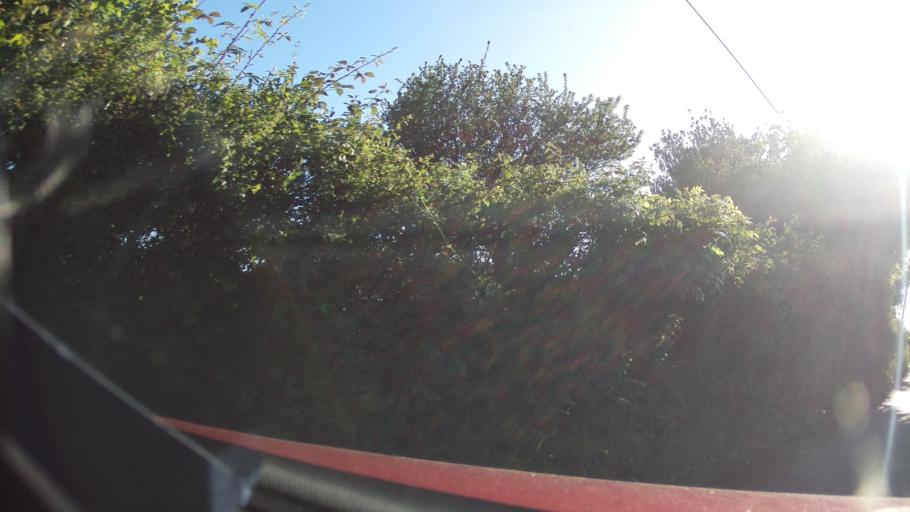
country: GB
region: England
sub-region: Dorset
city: Lyme Regis
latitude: 50.7933
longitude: -2.8792
